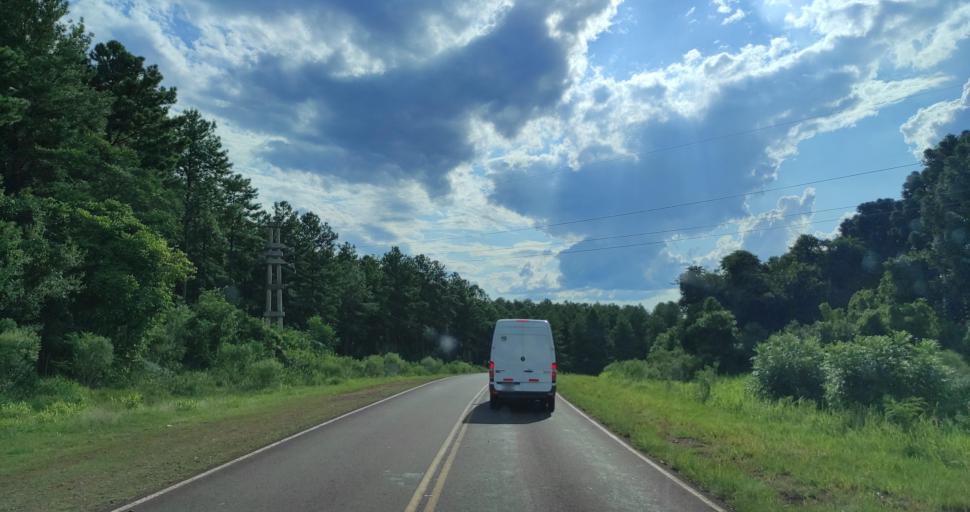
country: AR
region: Misiones
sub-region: Departamento de San Pedro
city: San Pedro
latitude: -26.3492
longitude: -53.9794
